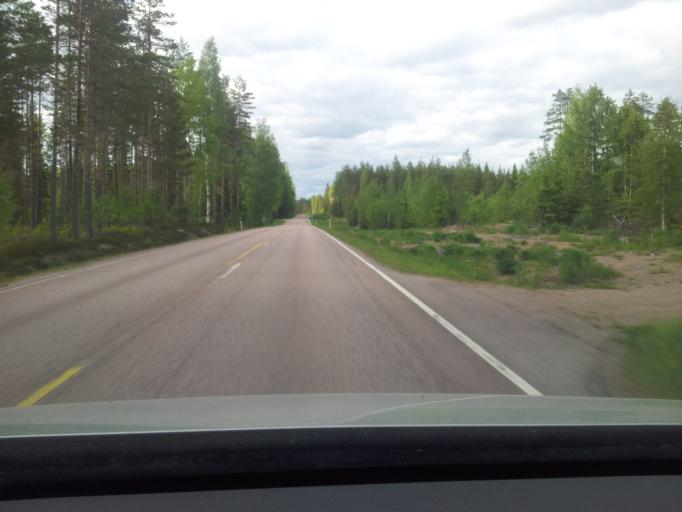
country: FI
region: South Karelia
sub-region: Lappeenranta
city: Luumaeki
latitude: 60.9387
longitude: 27.5835
